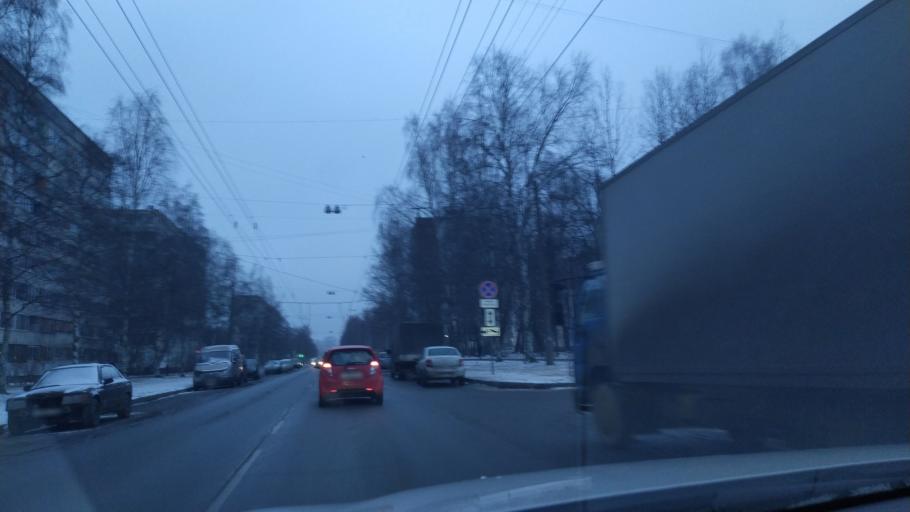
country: RU
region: Leningrad
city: Akademicheskoe
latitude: 60.0129
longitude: 30.4110
